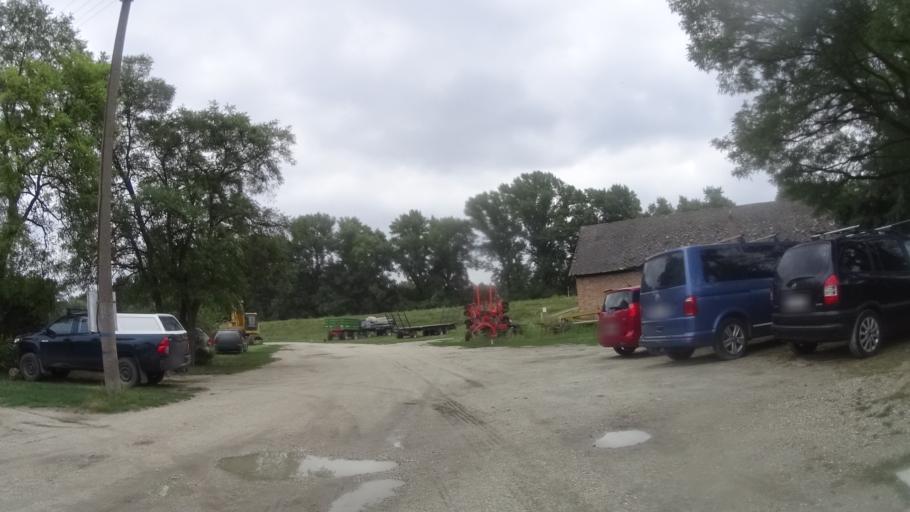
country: HU
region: Komarom-Esztergom
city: Acs
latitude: 47.7563
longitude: 17.9469
